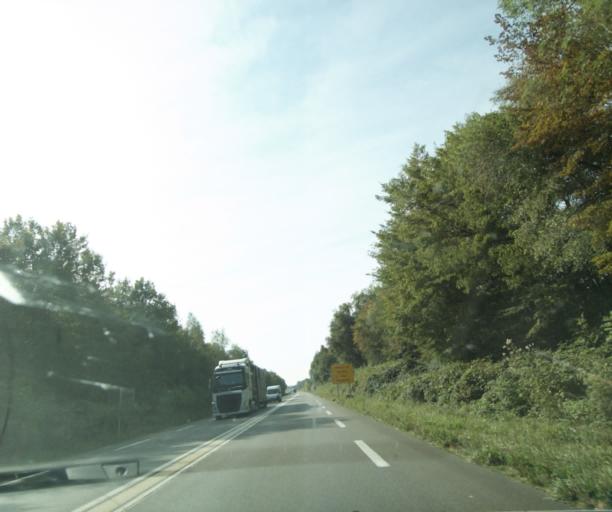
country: FR
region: Bourgogne
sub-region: Departement de Saone-et-Loire
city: Palinges
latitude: 46.5277
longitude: 4.1661
